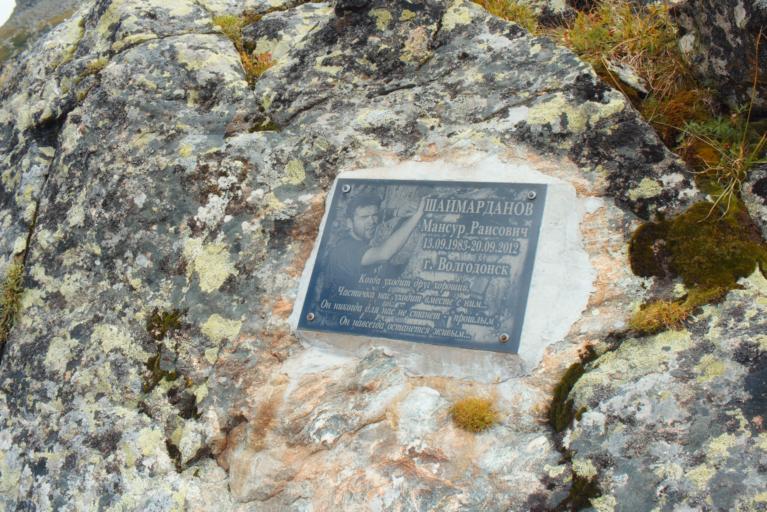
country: RU
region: Karachayevo-Cherkesiya
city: Nizhniy Arkhyz
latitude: 43.4384
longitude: 41.2572
